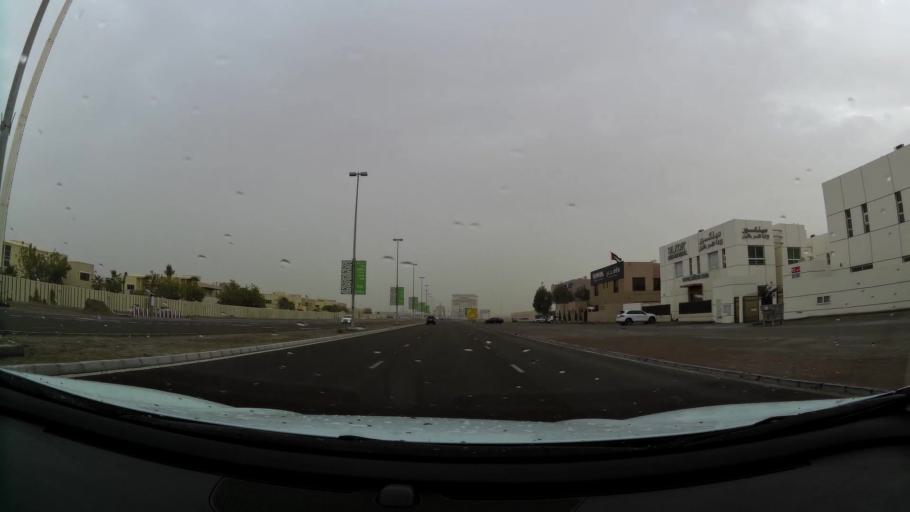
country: AE
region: Abu Dhabi
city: Abu Dhabi
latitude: 24.4402
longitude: 54.5986
